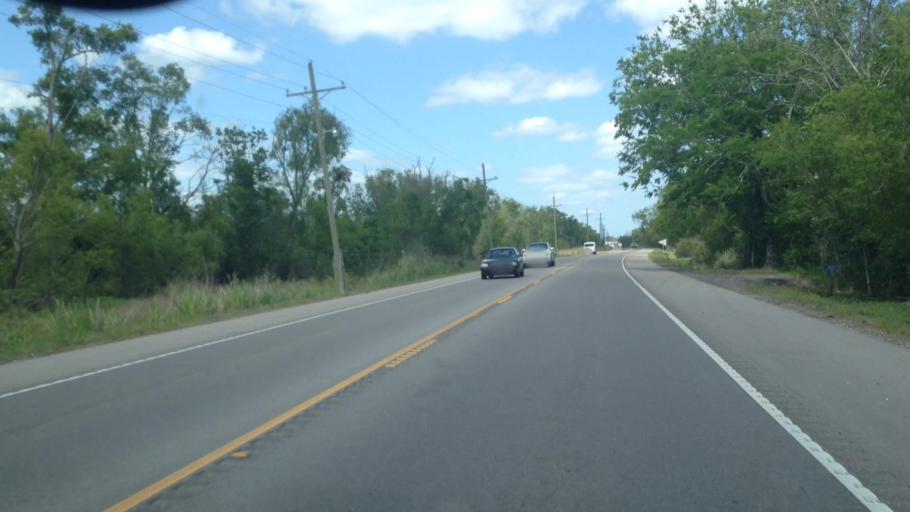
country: US
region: Louisiana
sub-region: Terrebonne Parish
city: Houma
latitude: 29.6352
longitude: -90.7001
